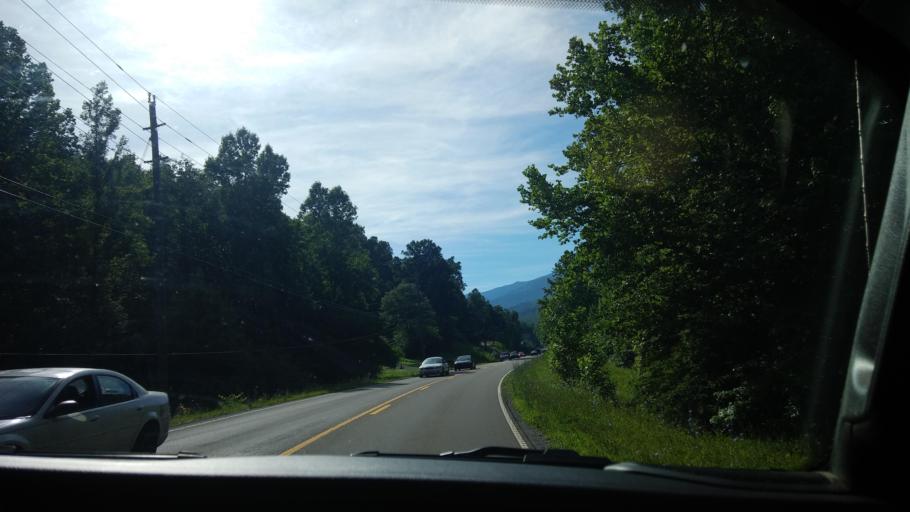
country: US
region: Tennessee
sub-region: Sevier County
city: Gatlinburg
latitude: 35.7615
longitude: -83.3723
